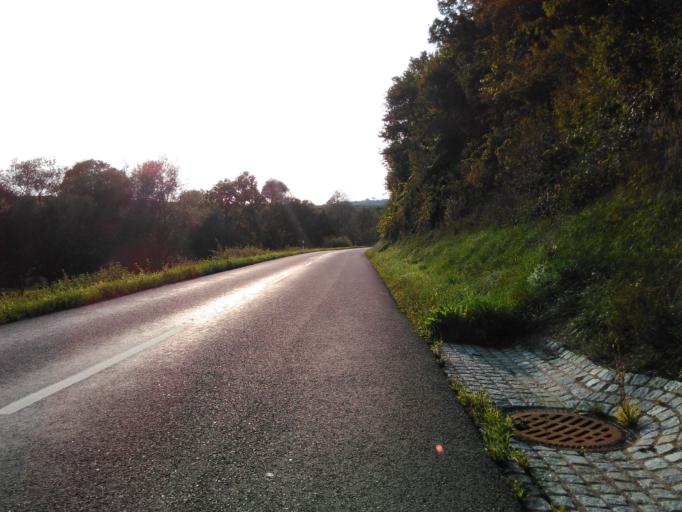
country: LU
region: Grevenmacher
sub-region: Canton de Remich
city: Lenningen
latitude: 49.6159
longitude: 6.3657
